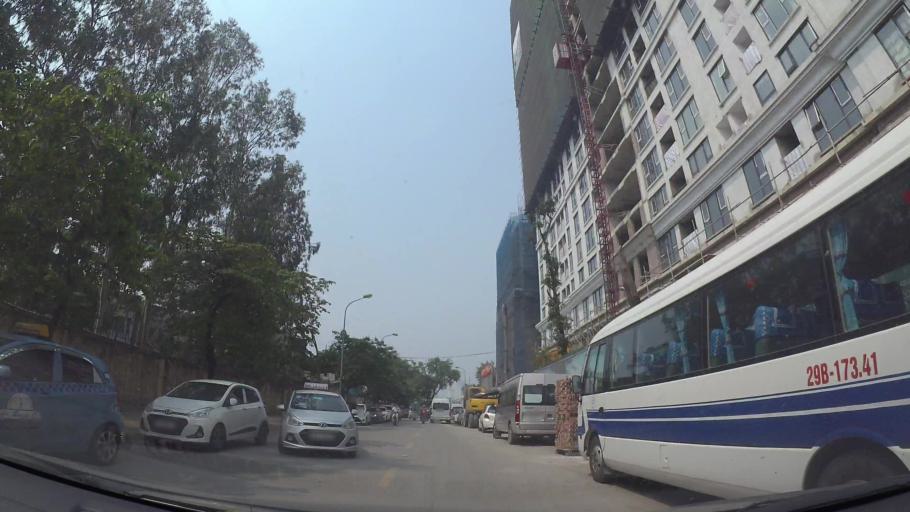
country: VN
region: Ha Noi
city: Dong Da
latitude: 21.0298
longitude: 105.8219
